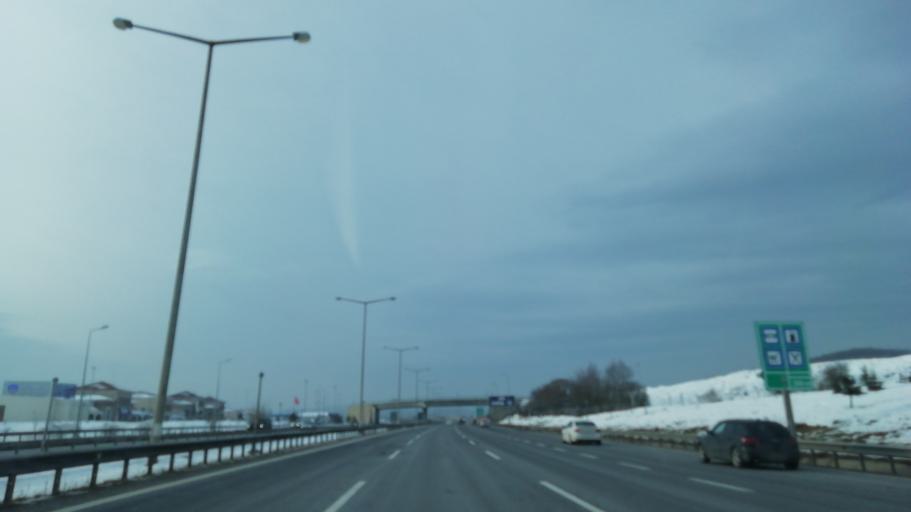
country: TR
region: Bolu
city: Bolu
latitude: 40.7227
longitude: 31.4719
